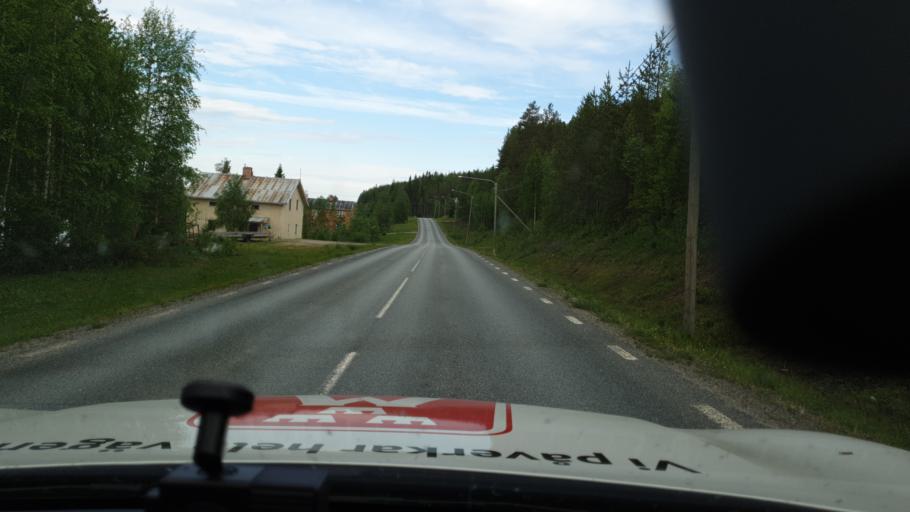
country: SE
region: Vaesterbotten
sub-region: Lycksele Kommun
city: Soderfors
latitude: 65.0901
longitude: 18.3245
